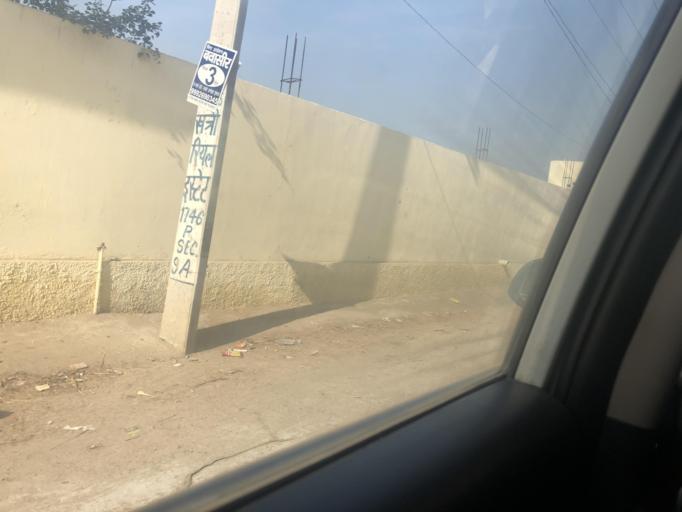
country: IN
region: Haryana
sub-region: Jhajjar
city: Bahadurgarh
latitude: 28.6867
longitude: 76.8972
